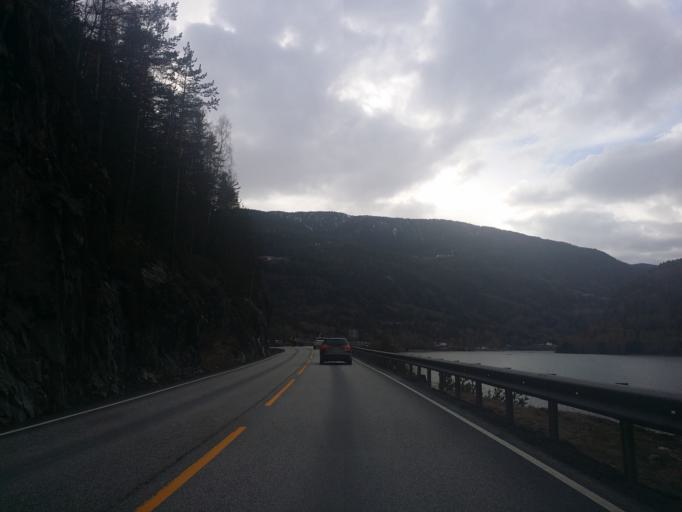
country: NO
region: Buskerud
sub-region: Nes
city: Nesbyen
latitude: 60.4879
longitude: 9.2139
